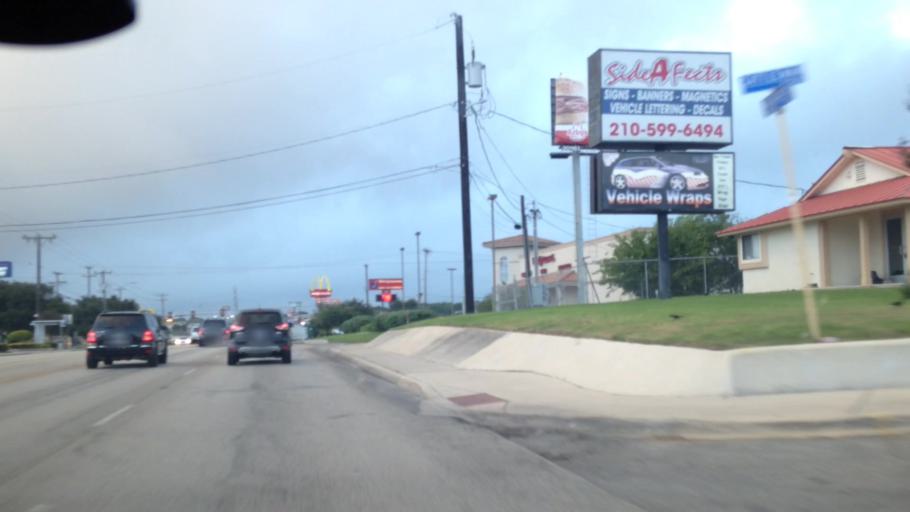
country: US
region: Texas
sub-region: Bexar County
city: Live Oak
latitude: 29.5695
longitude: -98.3835
